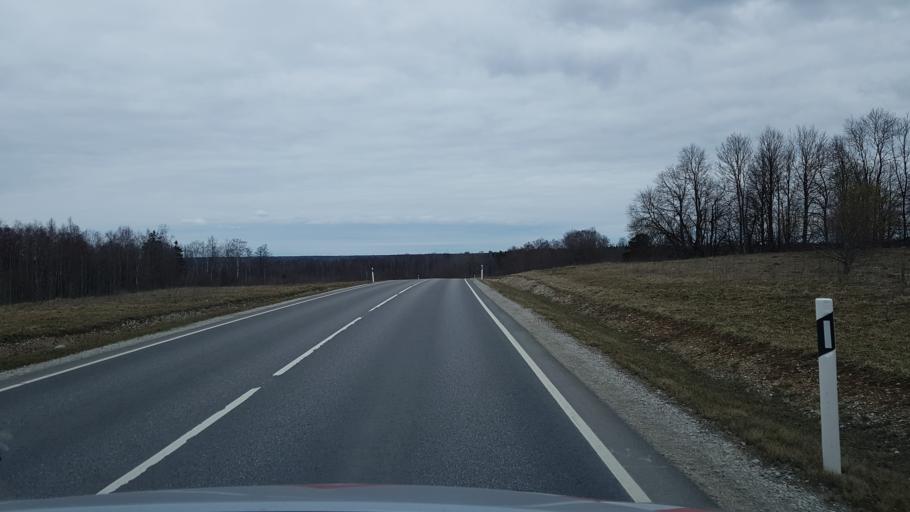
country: EE
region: Ida-Virumaa
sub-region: Narva-Joesuu linn
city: Narva-Joesuu
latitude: 59.4066
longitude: 28.0669
